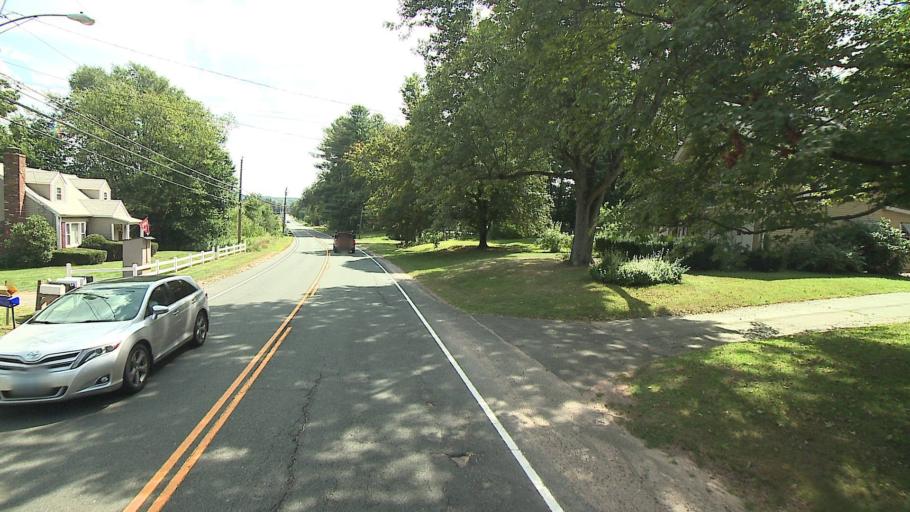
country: US
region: Connecticut
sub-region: Tolland County
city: Ellington
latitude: 41.9083
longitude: -72.4825
